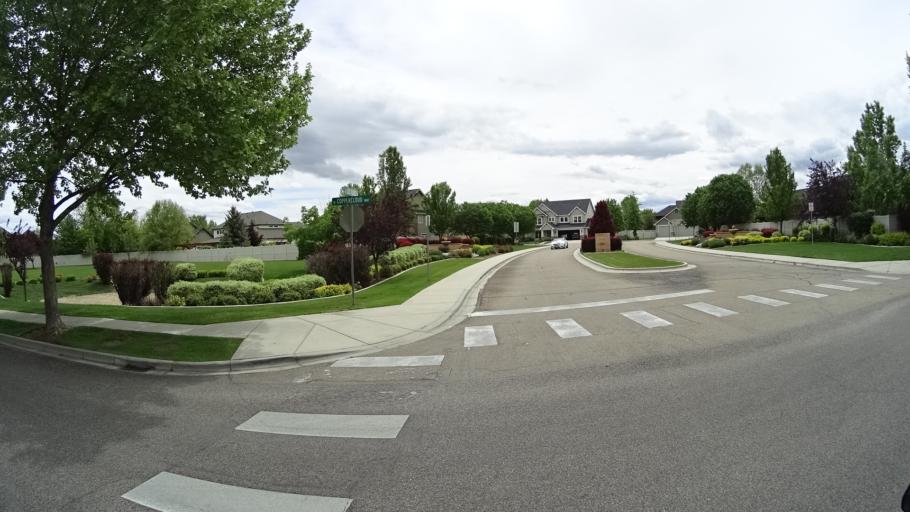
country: US
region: Idaho
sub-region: Ada County
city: Meridian
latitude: 43.6455
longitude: -116.4214
